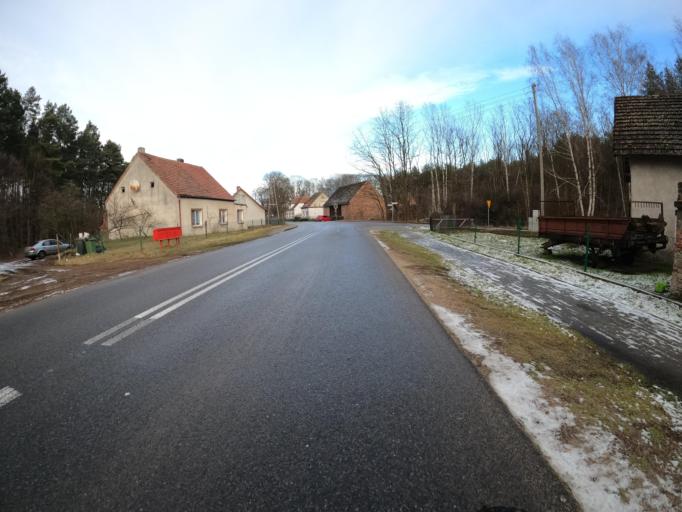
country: PL
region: Lubusz
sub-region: Powiat slubicki
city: Cybinka
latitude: 52.2175
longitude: 14.8417
